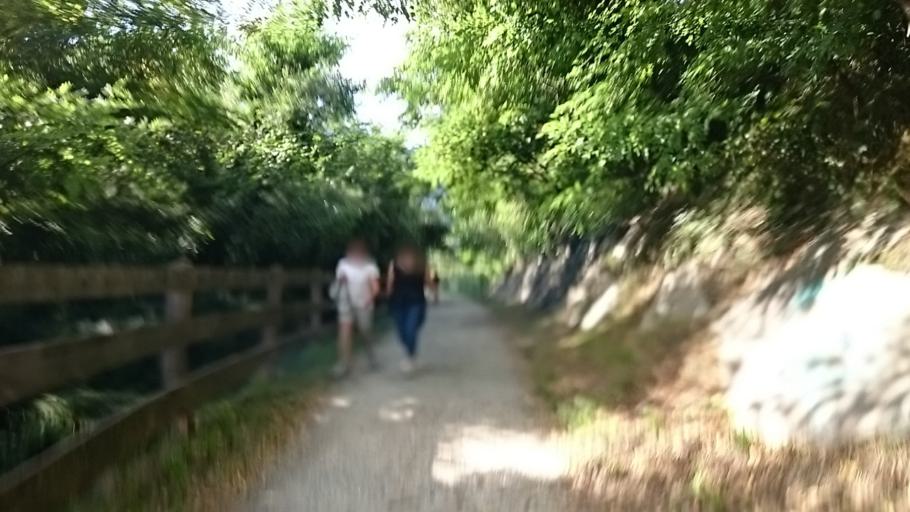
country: IT
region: Trentino-Alto Adige
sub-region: Bolzano
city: Leone-Santa Elisabetta
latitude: 46.7337
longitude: 11.6532
